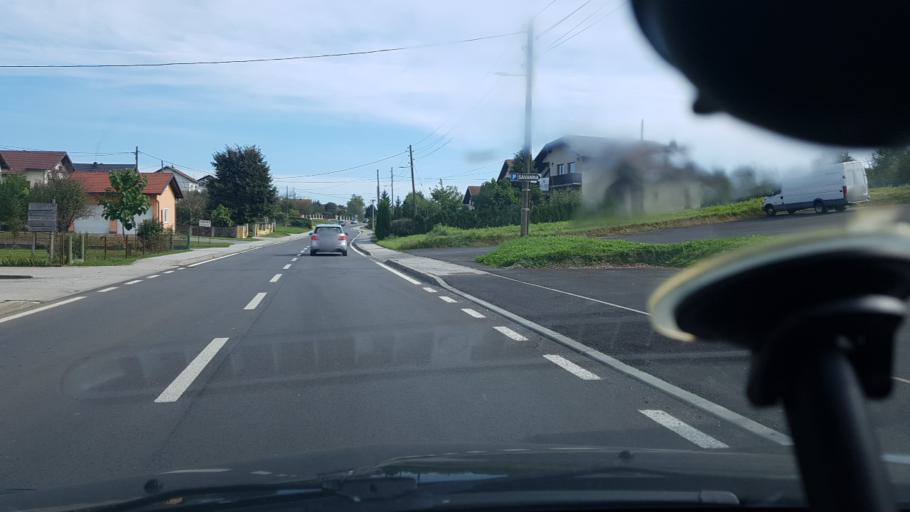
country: HR
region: Krapinsko-Zagorska
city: Marija Bistrica
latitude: 46.0560
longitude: 16.1796
